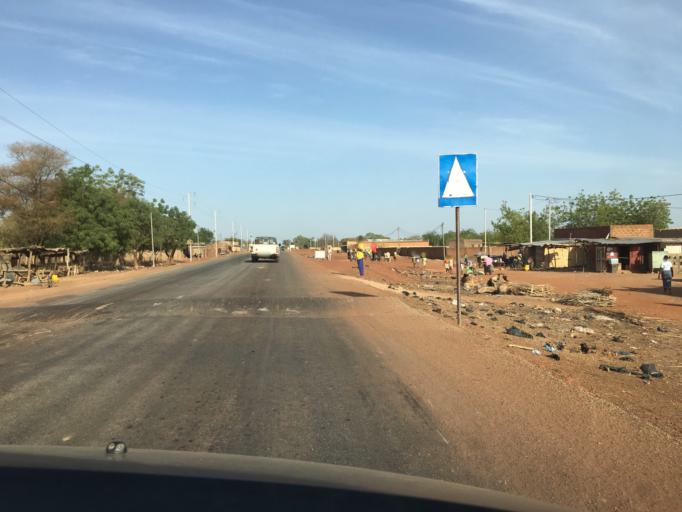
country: BF
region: Plateau-Central
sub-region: Province du Kourweogo
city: Bousse
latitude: 12.5323
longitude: -1.7785
